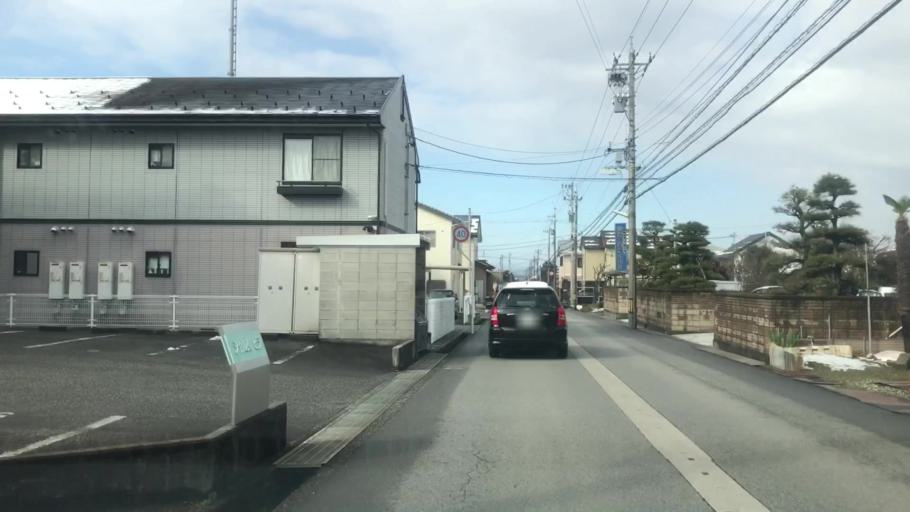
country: JP
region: Toyama
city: Toyama-shi
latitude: 36.6499
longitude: 137.2260
